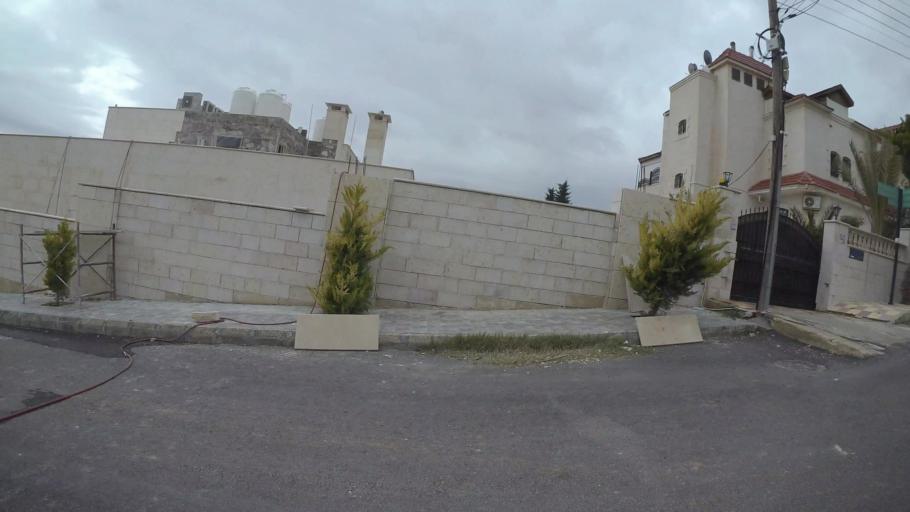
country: JO
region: Amman
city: Wadi as Sir
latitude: 31.9905
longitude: 35.8349
